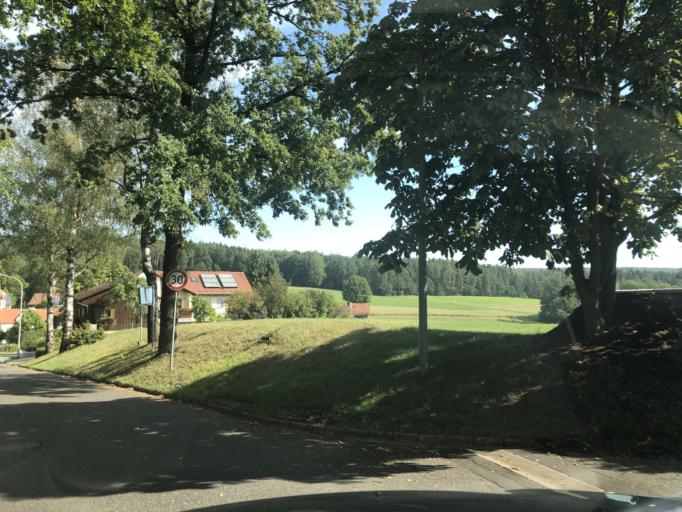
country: DE
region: Bavaria
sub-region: Upper Palatinate
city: Trabitz
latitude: 49.7916
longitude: 11.9220
